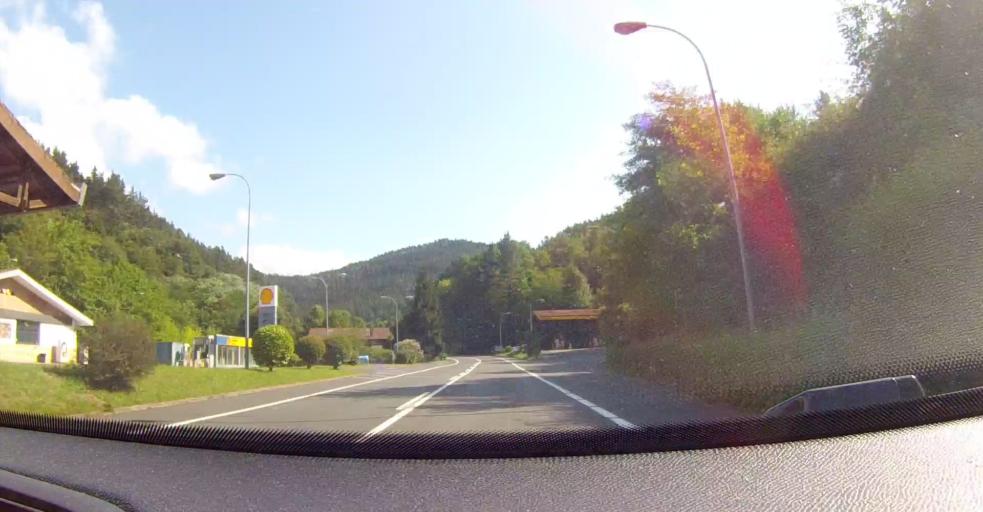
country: ES
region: Basque Country
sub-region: Bizkaia
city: Muxika
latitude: 43.2663
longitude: -2.6861
